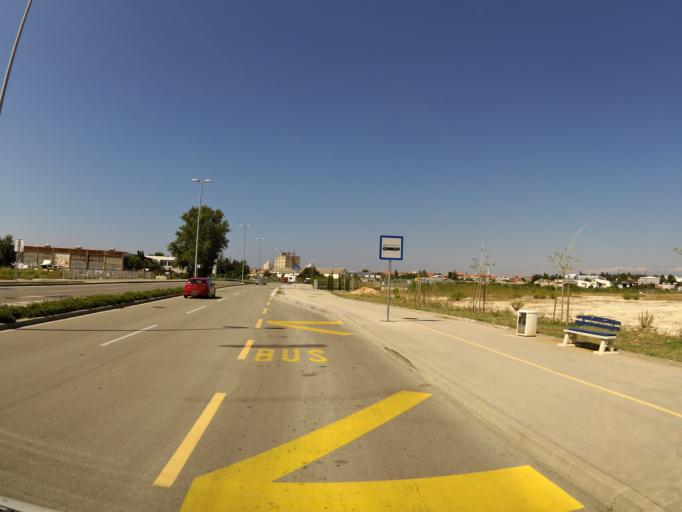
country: HR
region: Zadarska
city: Zadar
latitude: 44.0971
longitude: 15.2576
